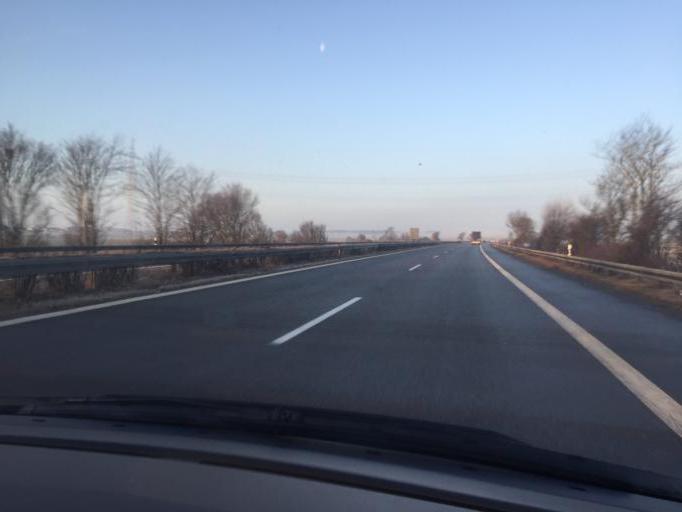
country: DE
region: Baden-Wuerttemberg
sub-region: Freiburg Region
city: Tuningen
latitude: 47.9939
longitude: 8.5807
